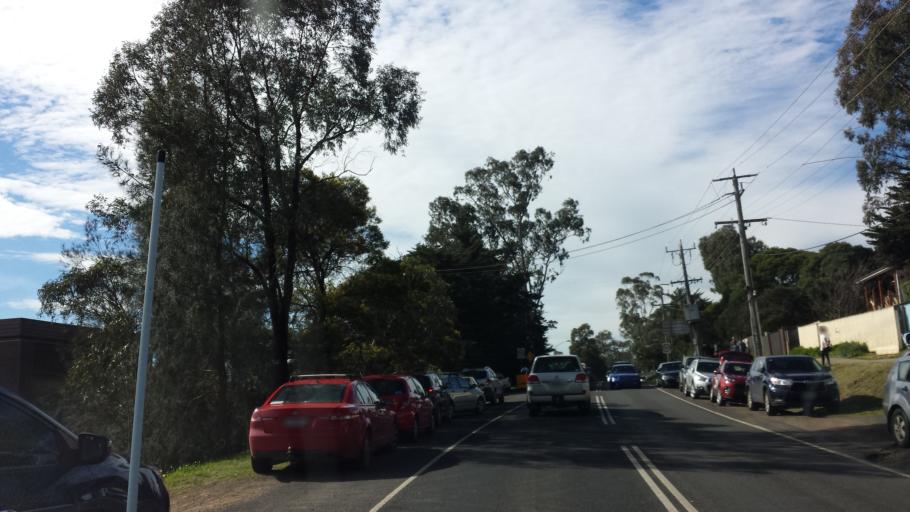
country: AU
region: Victoria
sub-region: Nillumbik
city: Hurstbridge
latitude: -37.6414
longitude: 145.1912
